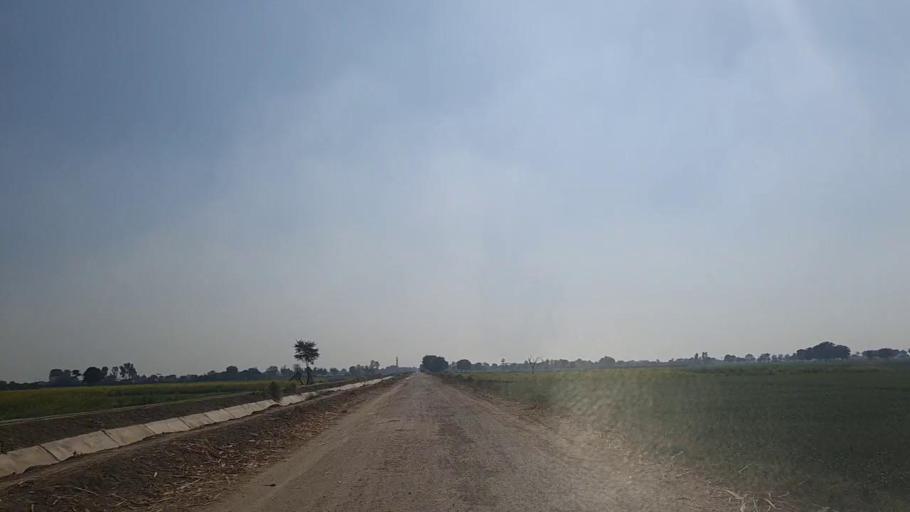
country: PK
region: Sindh
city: Shahpur Chakar
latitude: 26.1988
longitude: 68.5836
